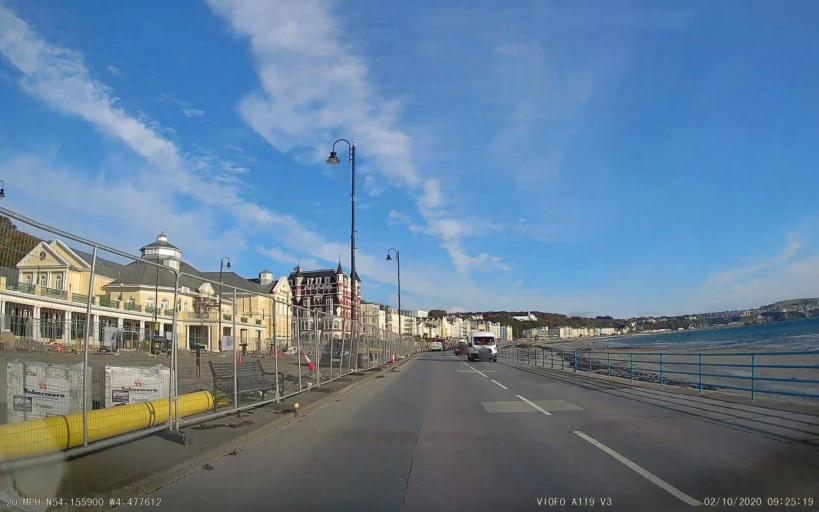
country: IM
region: Douglas
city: Douglas
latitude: 54.1559
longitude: -4.4775
